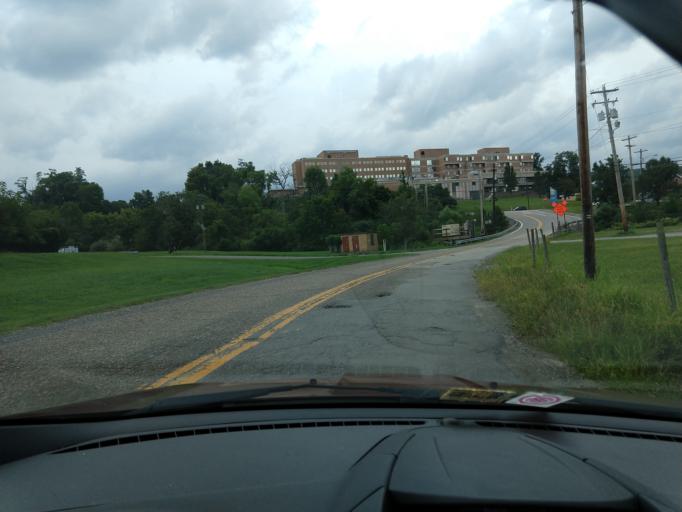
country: US
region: West Virginia
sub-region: Harrison County
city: Clarksburg
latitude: 39.2699
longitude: -80.3690
